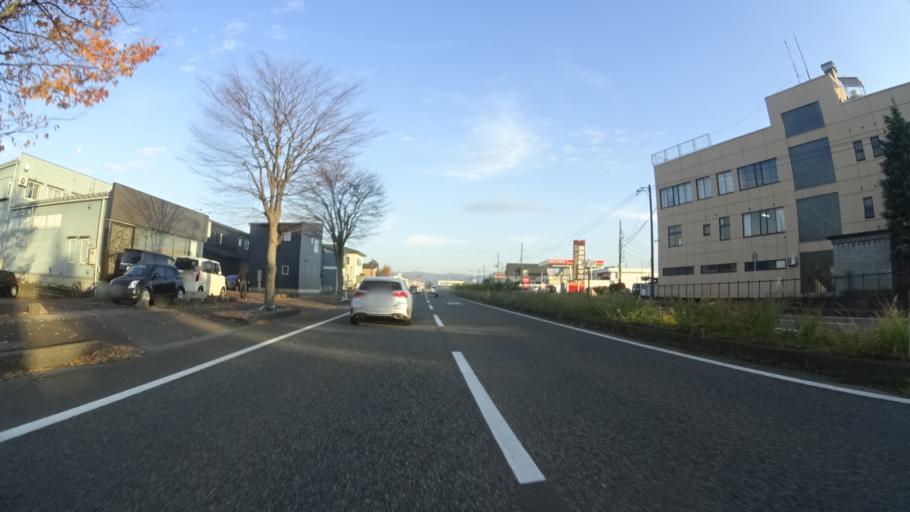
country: JP
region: Niigata
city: Nagaoka
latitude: 37.4473
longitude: 138.7732
